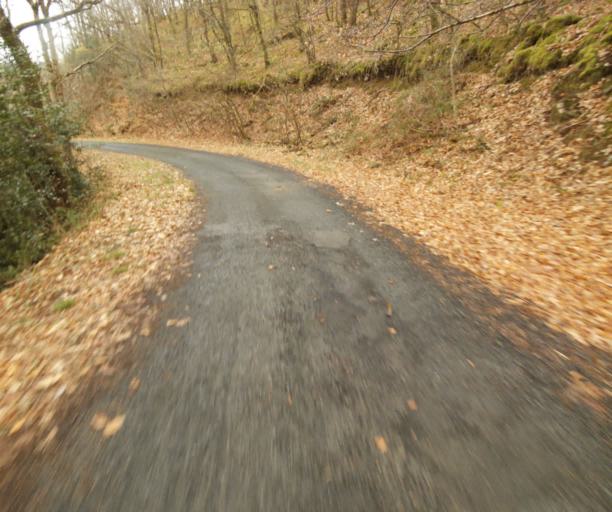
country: FR
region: Limousin
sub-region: Departement de la Correze
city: Saint-Privat
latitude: 45.2142
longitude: 2.0341
